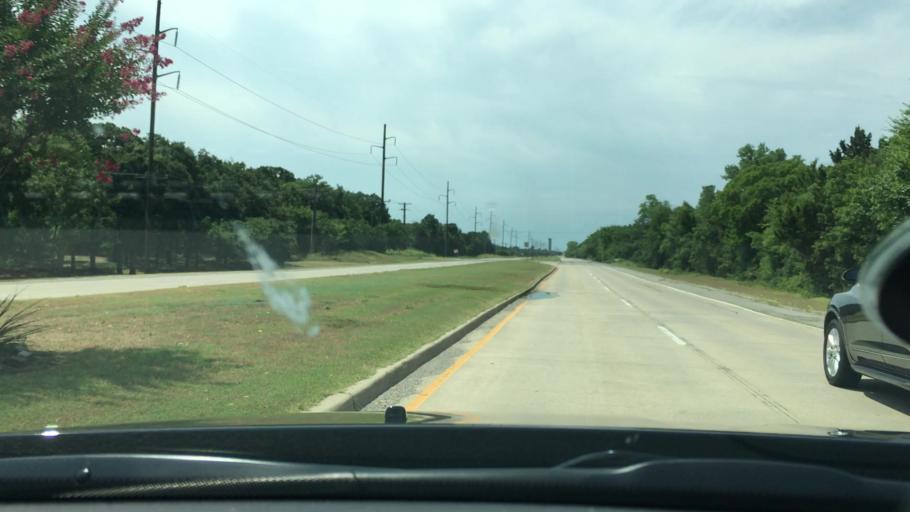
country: US
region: Oklahoma
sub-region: Carter County
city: Ardmore
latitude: 34.2183
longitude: -97.1432
